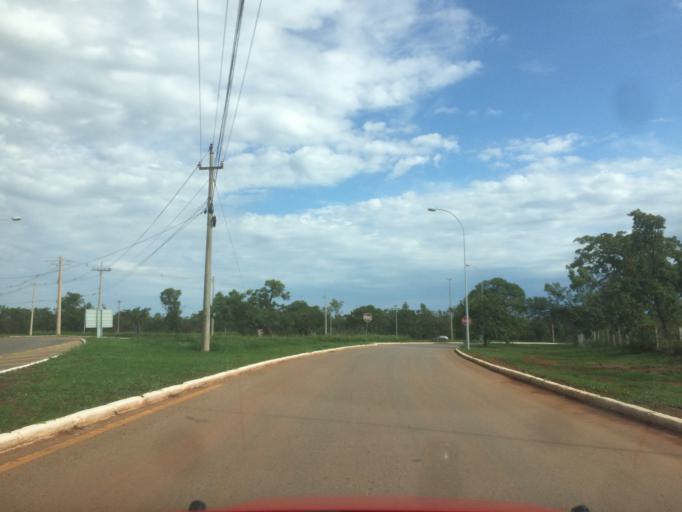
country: BR
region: Federal District
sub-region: Brasilia
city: Brasilia
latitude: -15.8078
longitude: -47.8380
